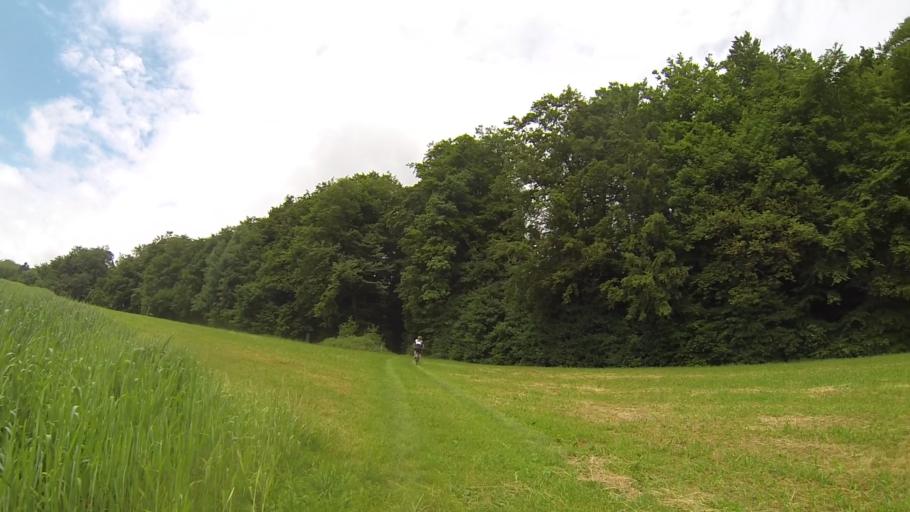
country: DE
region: Baden-Wuerttemberg
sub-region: Regierungsbezirk Stuttgart
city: Steinheim am Albuch
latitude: 48.6861
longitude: 10.0466
